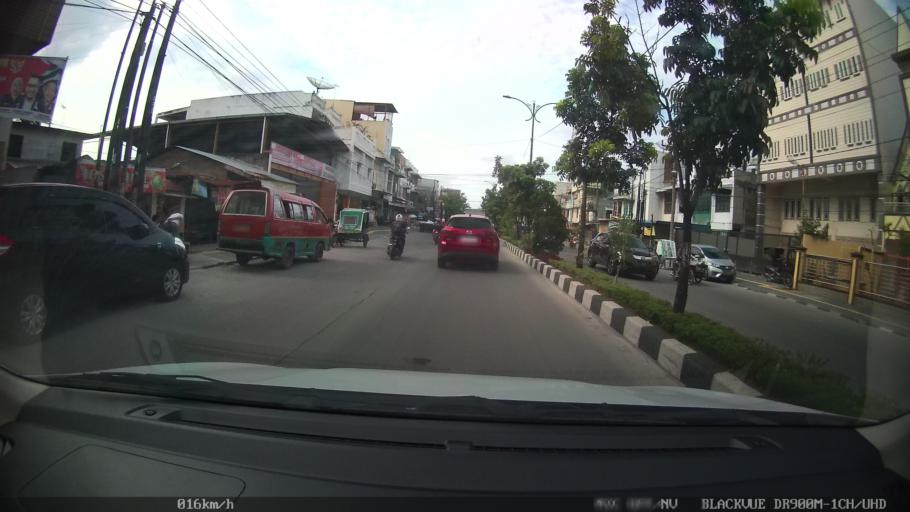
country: ID
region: North Sumatra
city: Medan
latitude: 3.6111
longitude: 98.6807
